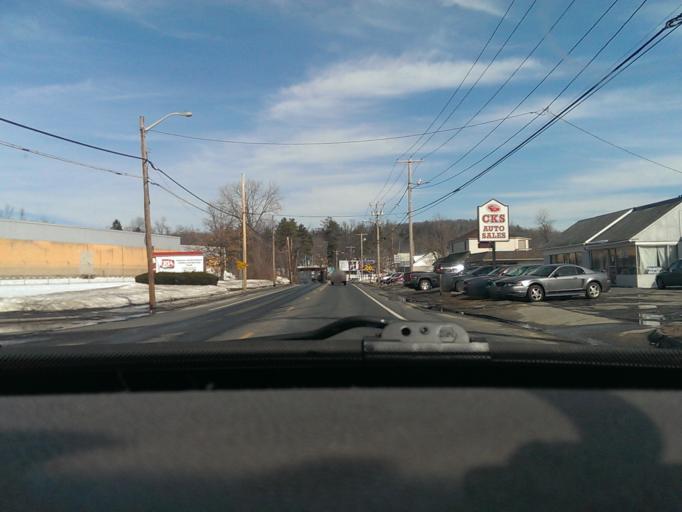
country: US
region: Massachusetts
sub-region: Hampden County
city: Palmer
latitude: 42.1617
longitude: -72.3481
